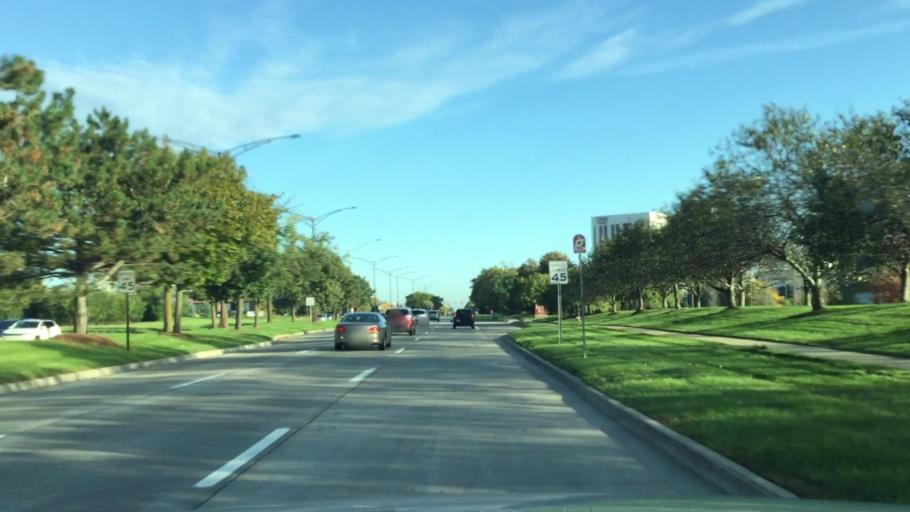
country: US
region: Michigan
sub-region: Oakland County
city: Troy
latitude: 42.5917
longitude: -83.1685
